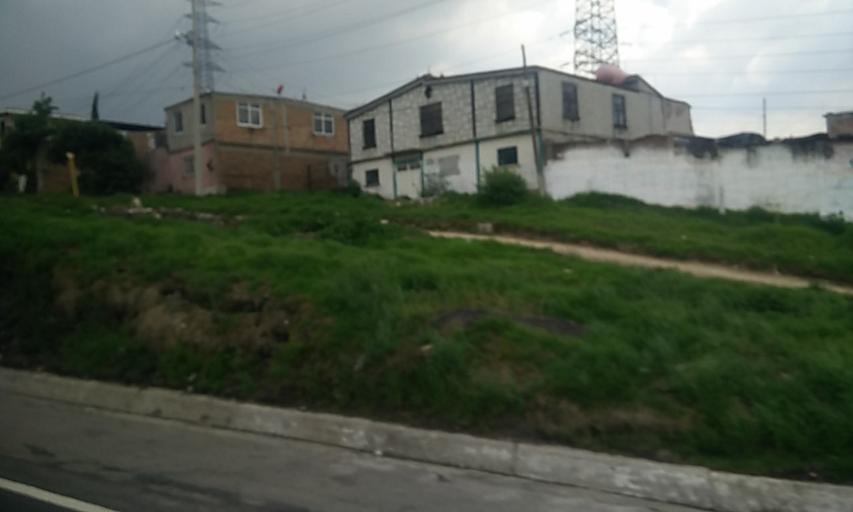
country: MX
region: Morelos
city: Coyotepec
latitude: 19.7792
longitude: -99.2196
